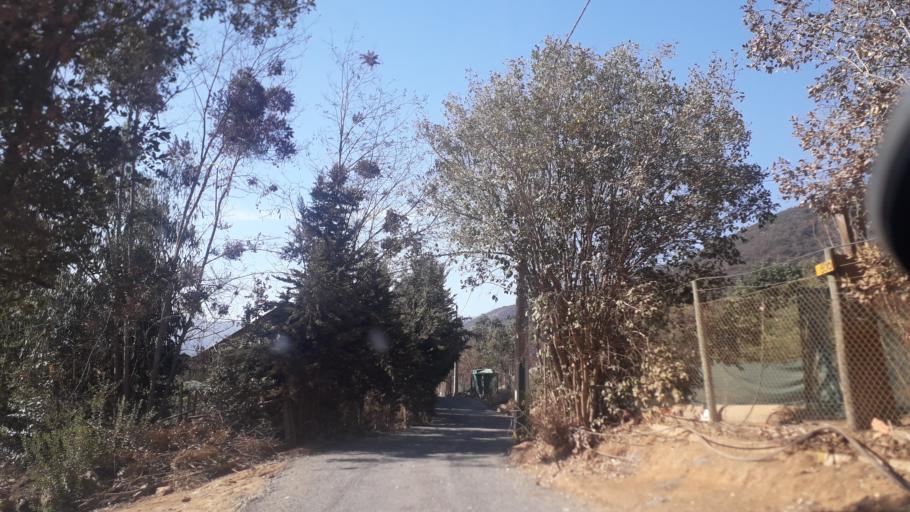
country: CL
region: Valparaiso
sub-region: Provincia de Marga Marga
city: Limache
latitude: -33.0816
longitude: -71.1003
